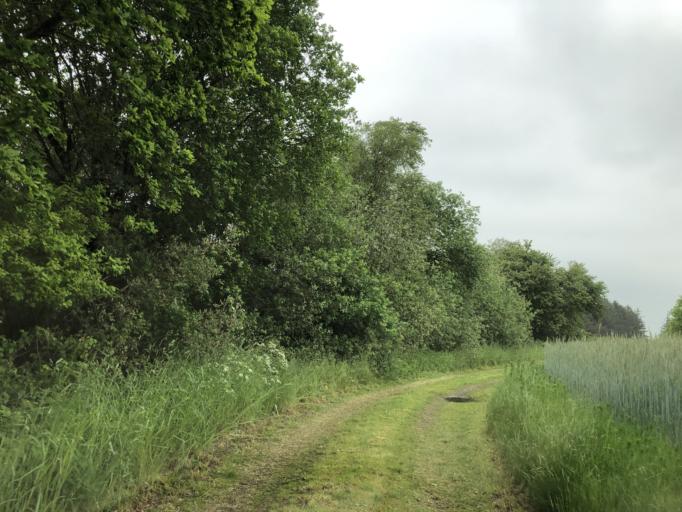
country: DK
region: Central Jutland
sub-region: Holstebro Kommune
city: Holstebro
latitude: 56.3324
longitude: 8.4808
